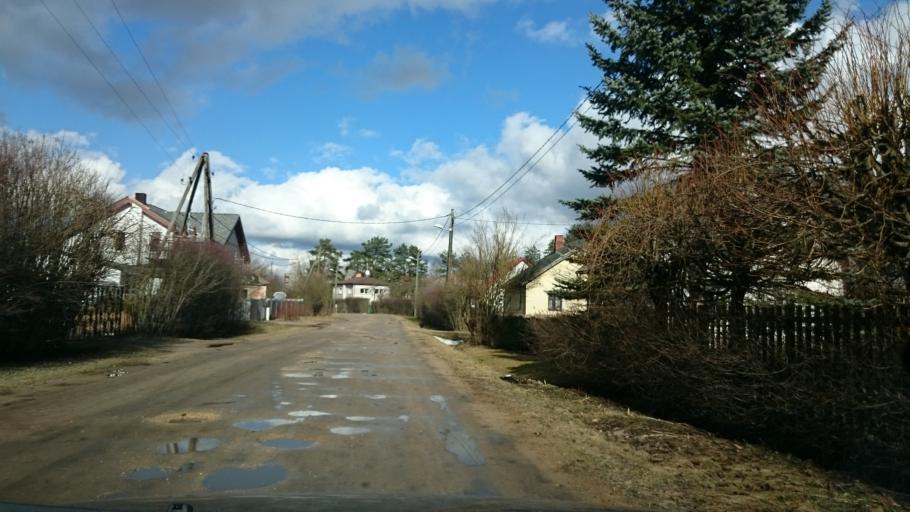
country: LV
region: Stopini
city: Ulbroka
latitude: 56.9557
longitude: 24.2873
